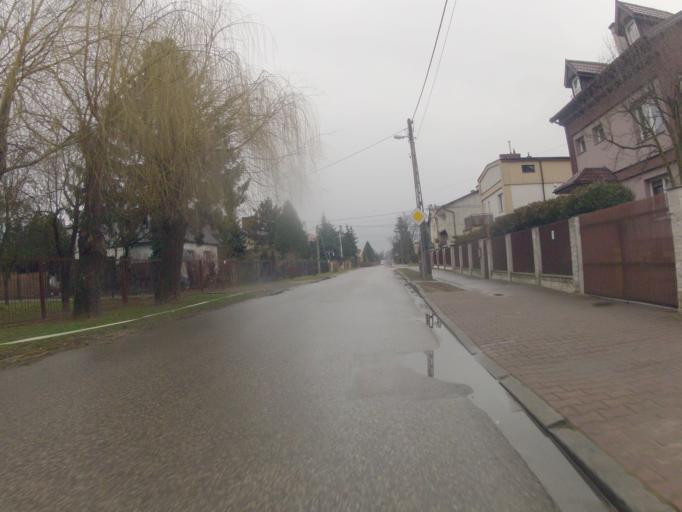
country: PL
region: Lesser Poland Voivodeship
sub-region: Powiat wielicki
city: Kokotow
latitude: 50.0576
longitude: 20.0455
